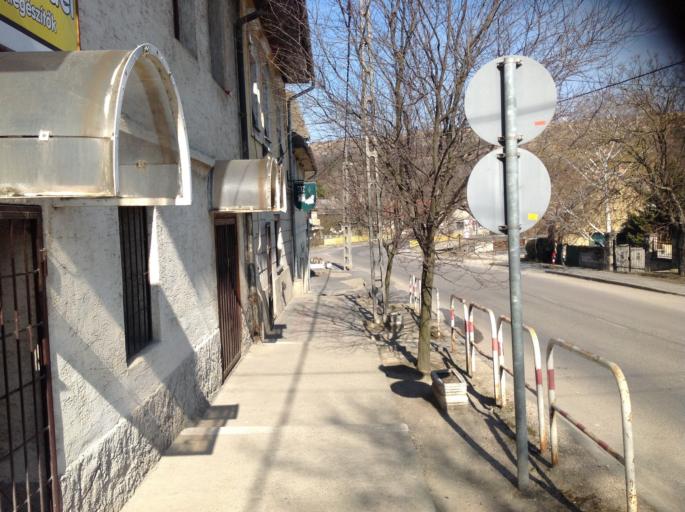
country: HU
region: Pest
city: Soskut
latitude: 47.4077
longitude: 18.8313
